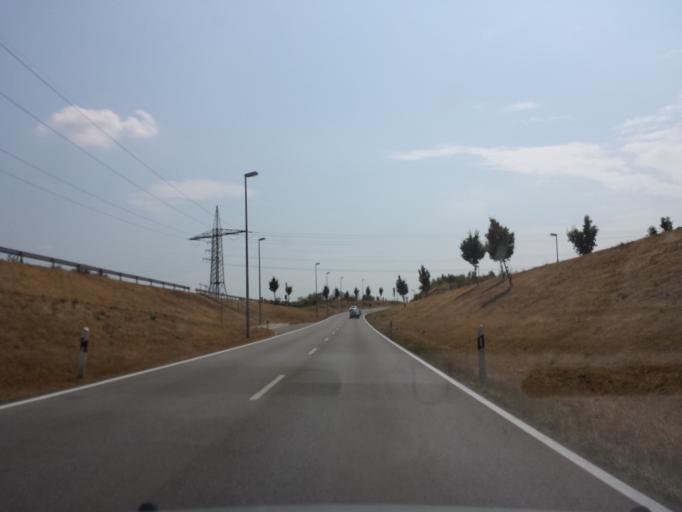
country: DE
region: Bavaria
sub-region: Swabia
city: Neu-Ulm
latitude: 48.4011
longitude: 10.0300
